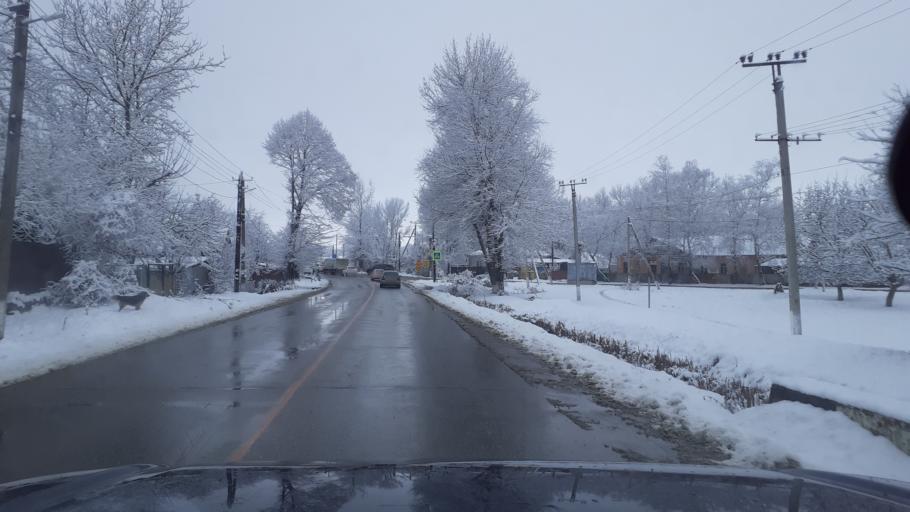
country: RU
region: Adygeya
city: Tul'skiy
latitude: 44.5061
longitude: 40.1705
